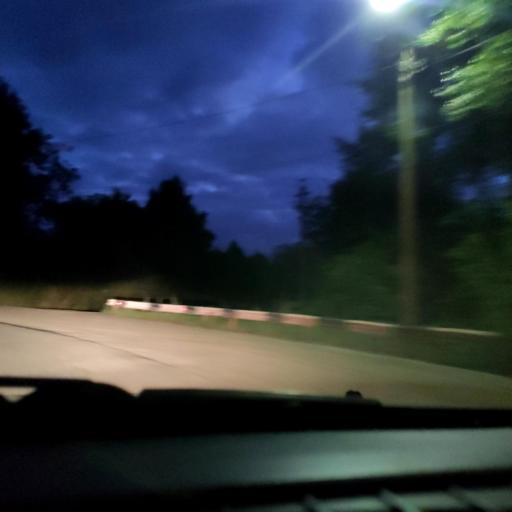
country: RU
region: Perm
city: Polazna
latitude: 58.1536
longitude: 56.4409
